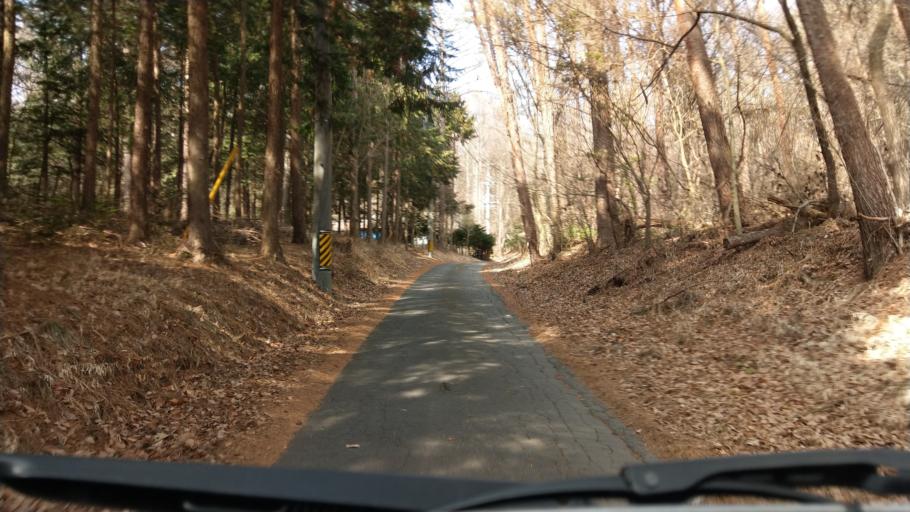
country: JP
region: Nagano
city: Komoro
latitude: 36.3356
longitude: 138.4639
